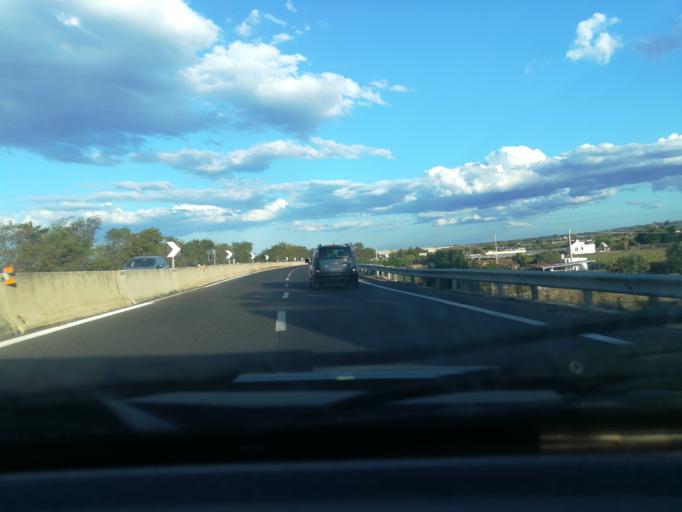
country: IT
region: Apulia
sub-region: Provincia di Bari
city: Mola di Bari
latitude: 41.0498
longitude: 17.0950
